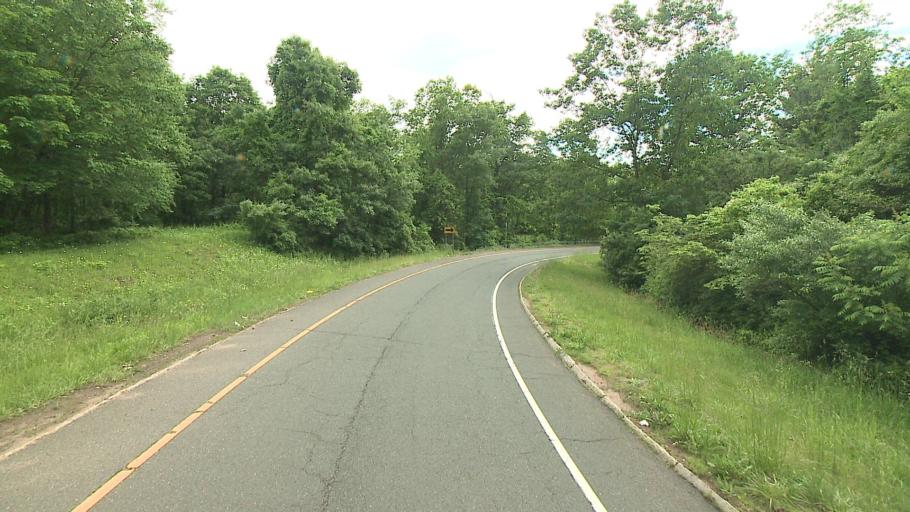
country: US
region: Connecticut
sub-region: New Haven County
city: Meriden
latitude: 41.5509
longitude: -72.8119
